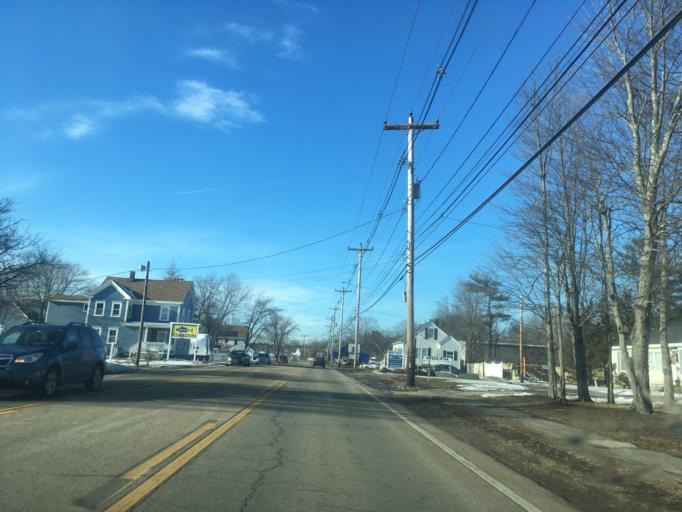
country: US
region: Massachusetts
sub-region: Essex County
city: Salisbury
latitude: 42.8410
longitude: -70.8685
